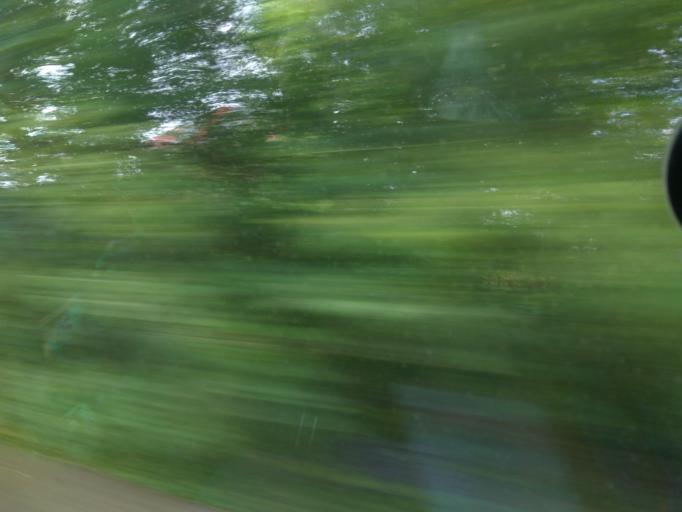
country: RU
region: Moskovskaya
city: Bronnitsy
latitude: 55.4719
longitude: 38.2645
